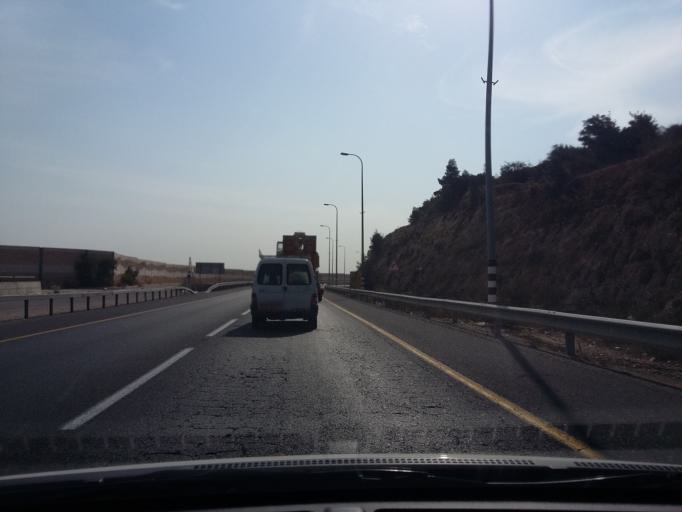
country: PS
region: West Bank
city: Al Khadir
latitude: 31.6936
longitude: 35.1583
